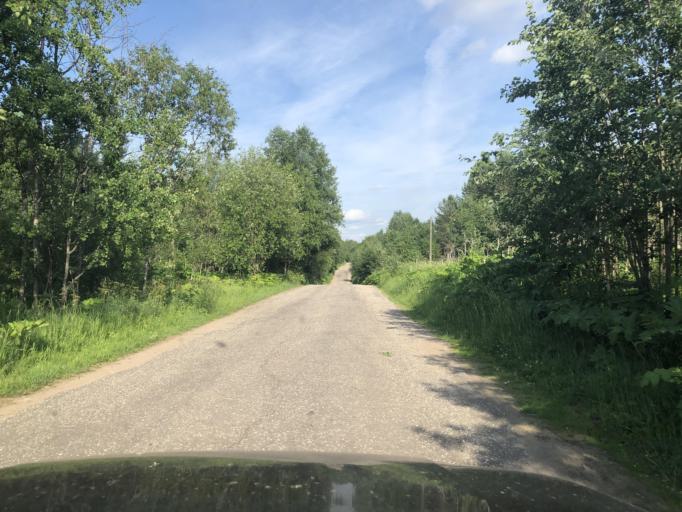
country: RU
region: Komi Republic
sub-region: Syktyvdinskiy Rayon
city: Syktyvkar
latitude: 61.6470
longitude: 50.7623
